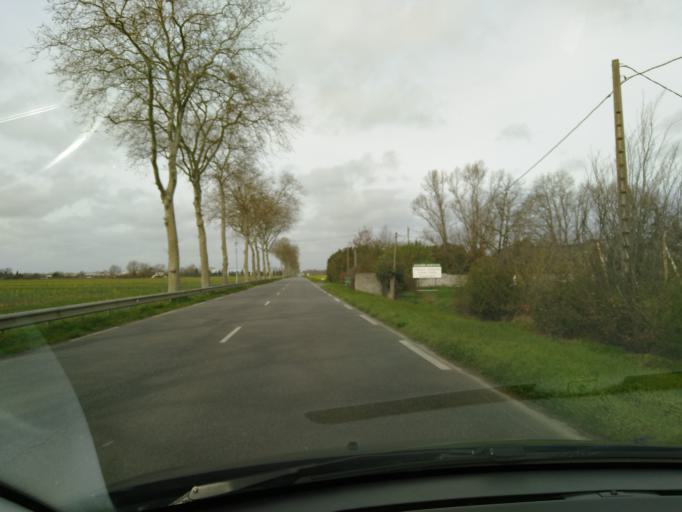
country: FR
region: Midi-Pyrenees
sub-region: Departement de la Haute-Garonne
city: Seilh
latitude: 43.7115
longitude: 1.3383
